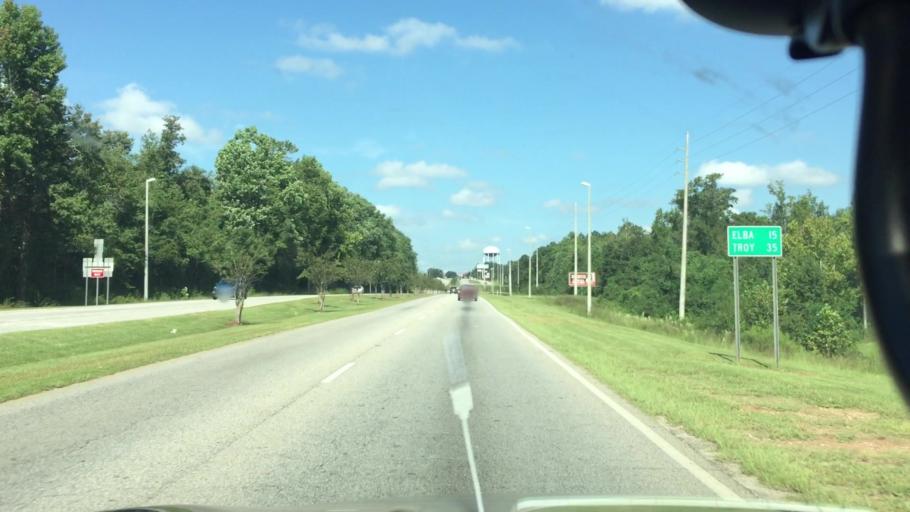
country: US
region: Alabama
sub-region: Coffee County
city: Enterprise
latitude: 31.3298
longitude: -85.8401
